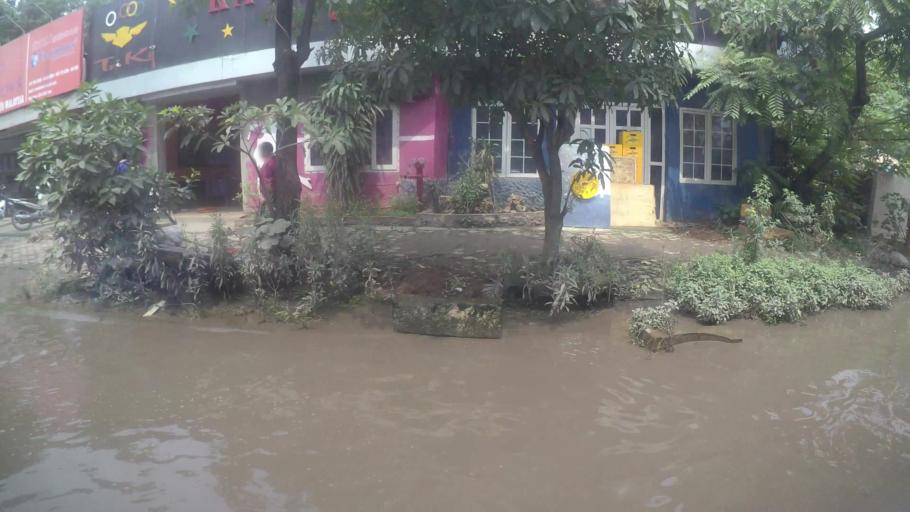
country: VN
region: Ha Noi
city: Tay Ho
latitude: 21.0801
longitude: 105.7880
